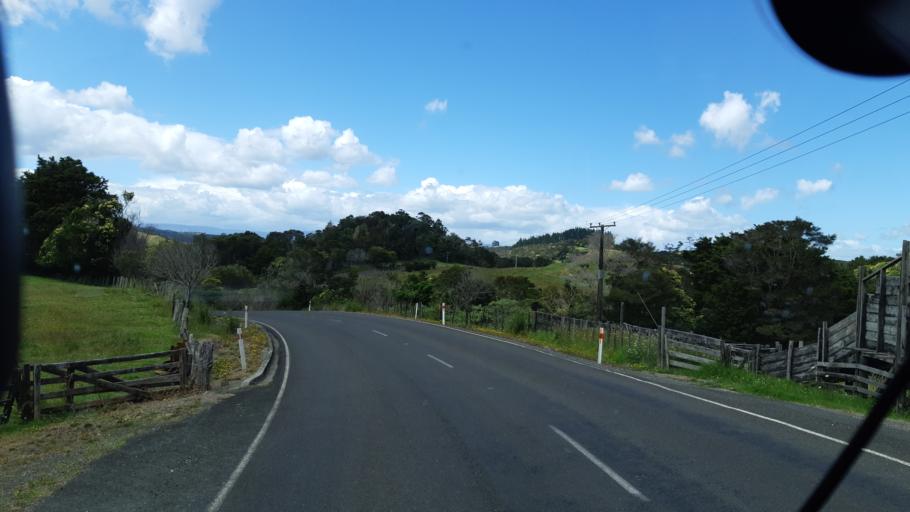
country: NZ
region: Northland
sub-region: Far North District
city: Taipa
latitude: -35.2652
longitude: 173.5242
